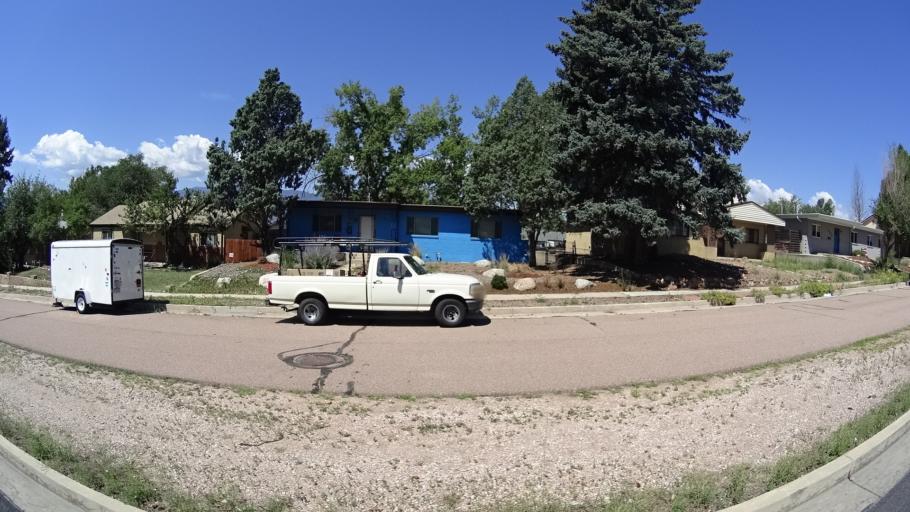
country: US
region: Colorado
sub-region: El Paso County
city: Colorado Springs
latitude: 38.8635
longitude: -104.7943
